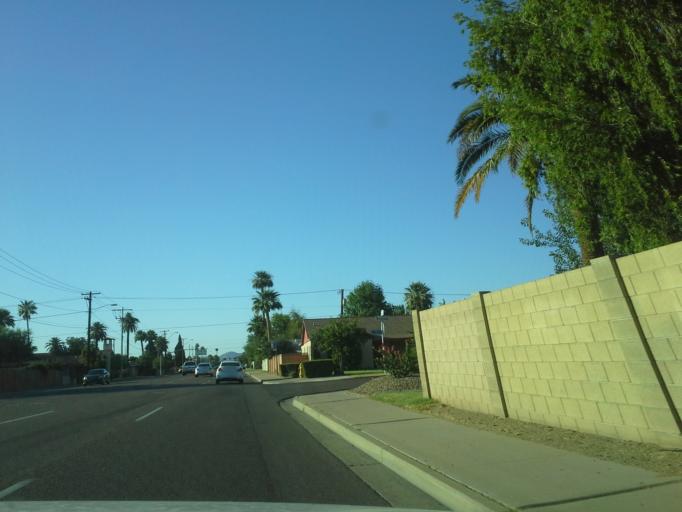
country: US
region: Arizona
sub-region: Maricopa County
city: Phoenix
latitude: 33.4764
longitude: -112.0829
